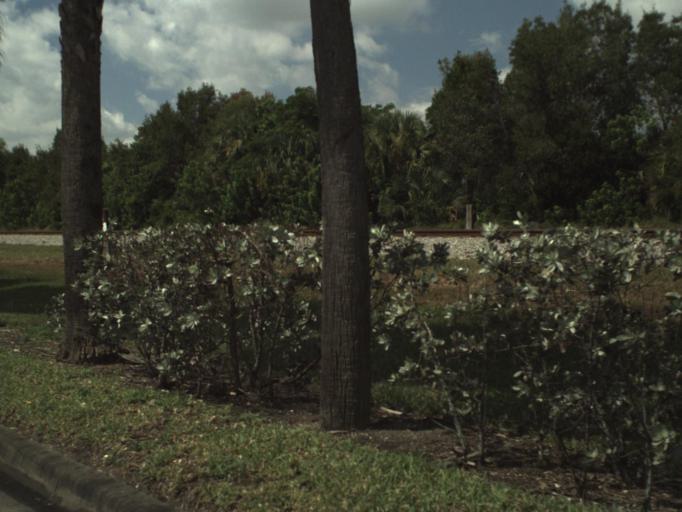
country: US
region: Florida
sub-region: Palm Beach County
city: North Palm Beach
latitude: 26.8334
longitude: -80.0925
